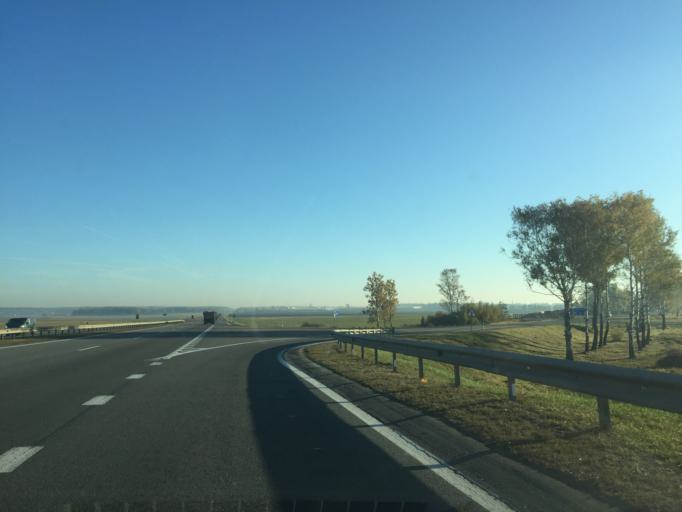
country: BY
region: Minsk
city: Pryvol'ny
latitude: 53.8169
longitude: 27.8196
